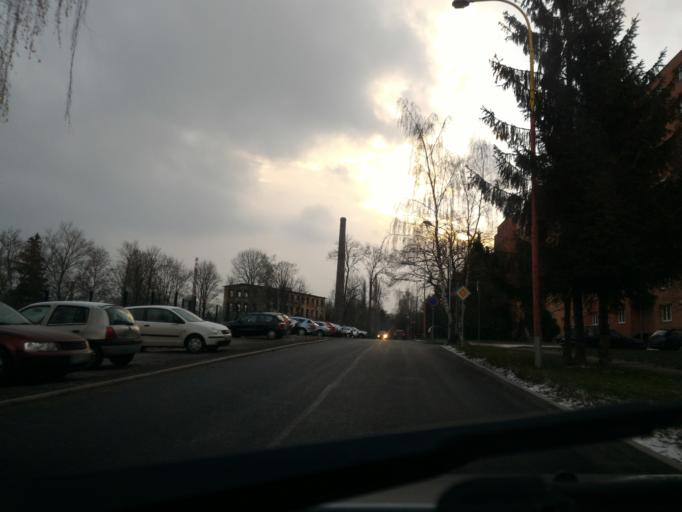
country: CZ
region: Ustecky
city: Varnsdorf
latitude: 50.9068
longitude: 14.6246
